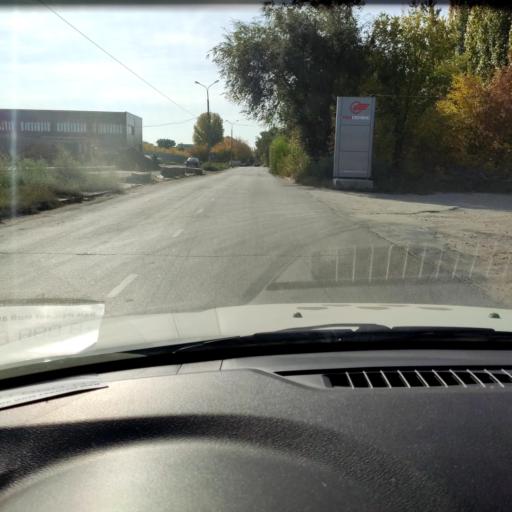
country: RU
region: Samara
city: Tol'yatti
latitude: 53.5577
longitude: 49.3099
